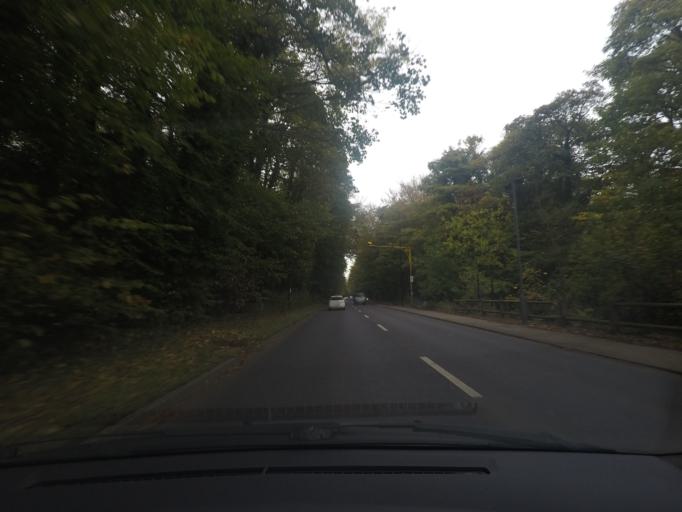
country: GB
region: England
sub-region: Sheffield
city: Chapletown
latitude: 53.4465
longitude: -1.4953
